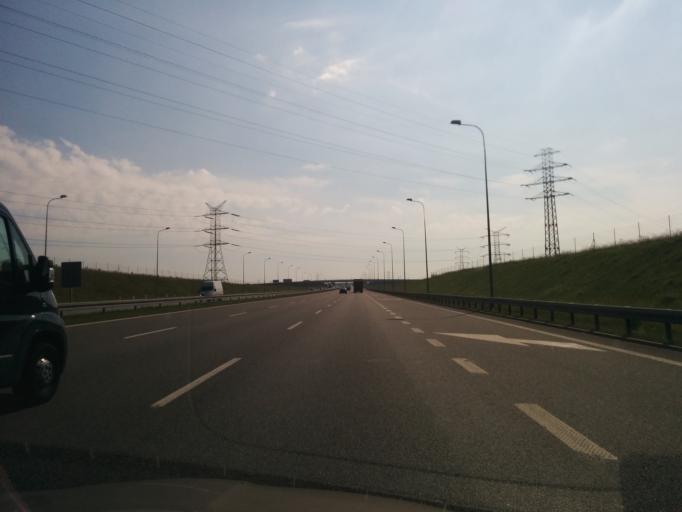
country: PL
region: Silesian Voivodeship
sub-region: Powiat tarnogorski
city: Wieszowa
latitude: 50.3718
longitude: 18.7473
